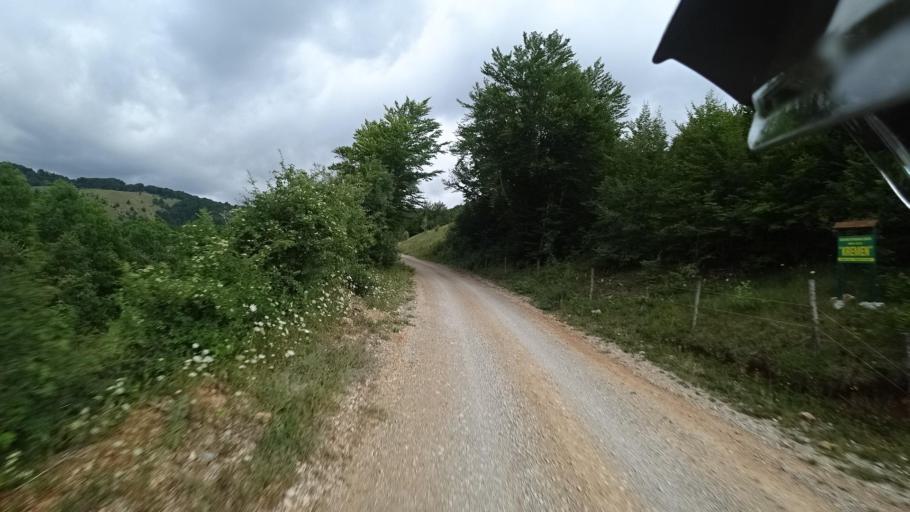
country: HR
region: Zadarska
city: Gracac
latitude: 44.5196
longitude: 15.8547
